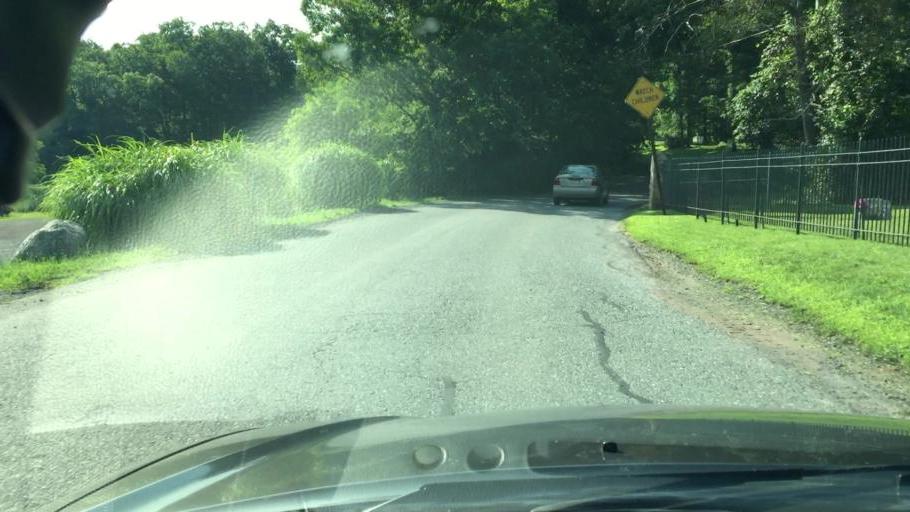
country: US
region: Pennsylvania
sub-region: Carbon County
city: Jim Thorpe
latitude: 40.8765
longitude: -75.7431
